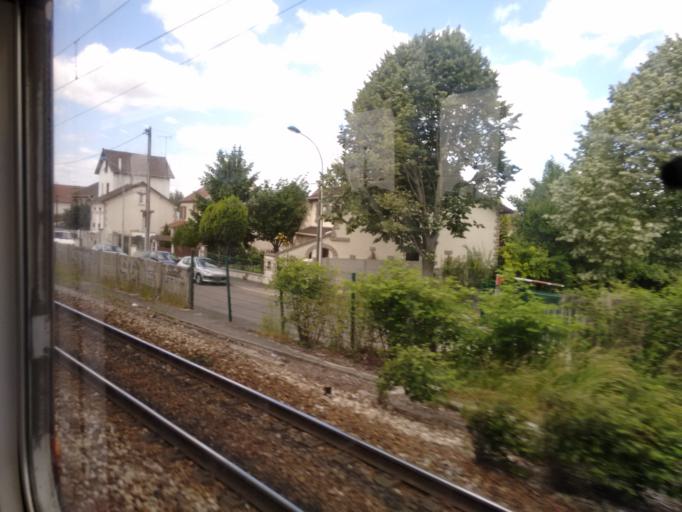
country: FR
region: Ile-de-France
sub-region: Departement de Seine-Saint-Denis
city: Le Blanc-Mesnil
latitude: 48.9324
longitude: 2.4723
